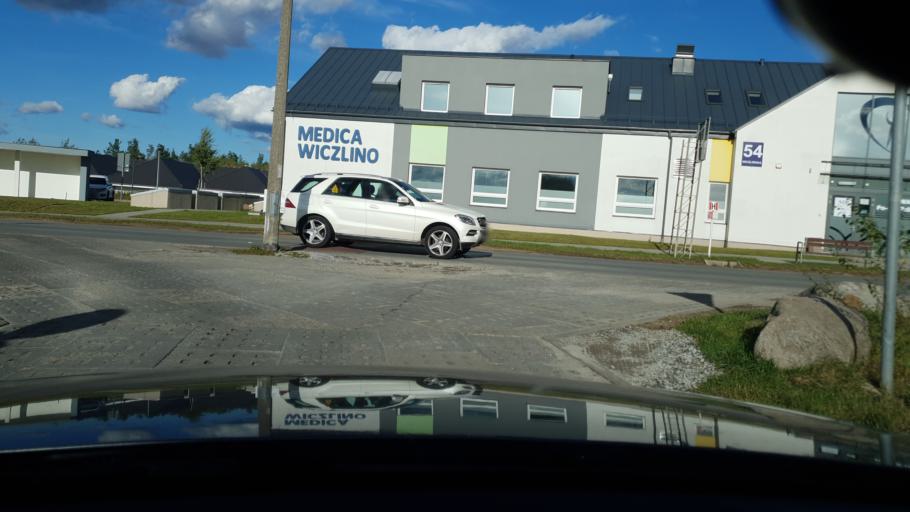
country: PL
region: Pomeranian Voivodeship
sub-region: Powiat wejherowski
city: Bojano
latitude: 54.4895
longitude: 18.4251
